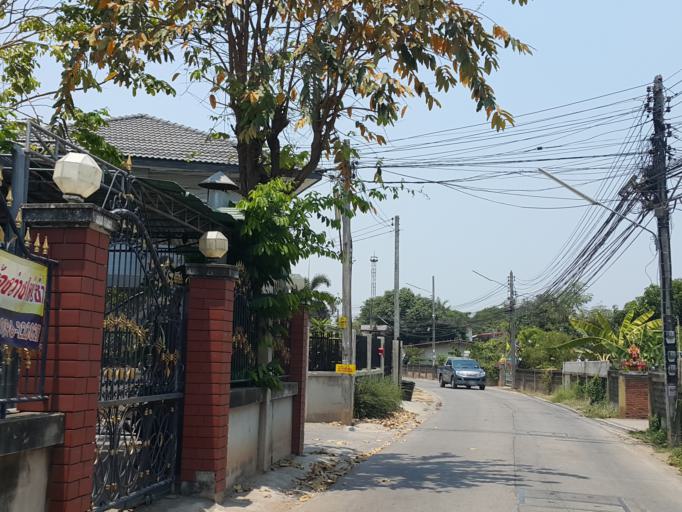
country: TH
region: Phitsanulok
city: Phitsanulok
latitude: 16.8155
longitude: 100.2519
